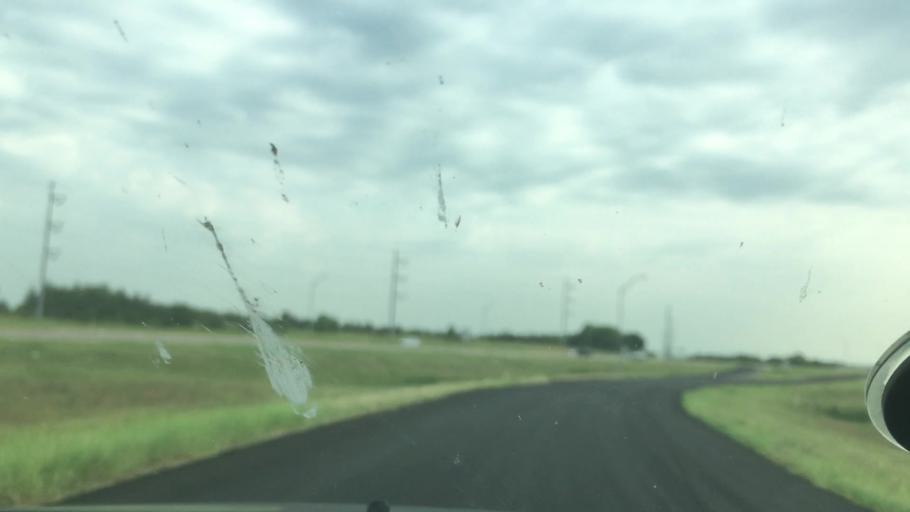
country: US
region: Texas
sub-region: Grayson County
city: Denison
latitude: 33.7812
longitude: -96.5820
